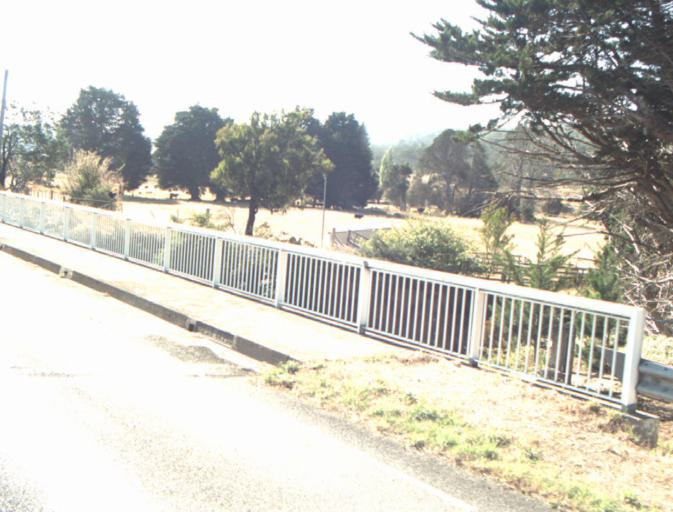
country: AU
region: Tasmania
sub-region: Launceston
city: Mayfield
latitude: -41.3308
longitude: 147.0729
